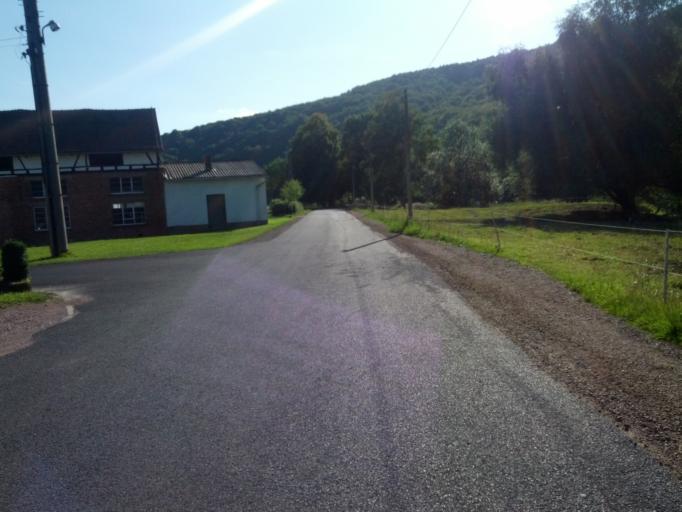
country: DE
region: Thuringia
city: Frankenroda
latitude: 51.0735
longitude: 10.2734
